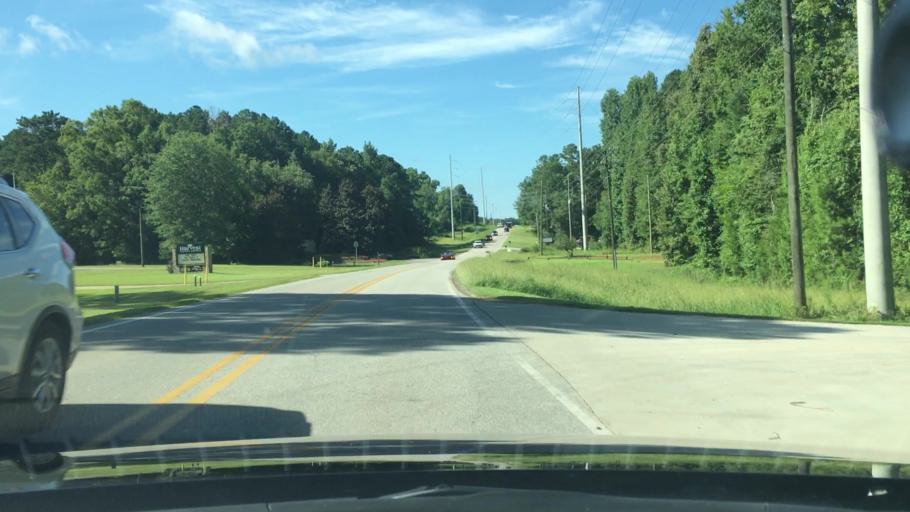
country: US
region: Georgia
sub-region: Putnam County
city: Jefferson
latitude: 33.4169
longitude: -83.2672
